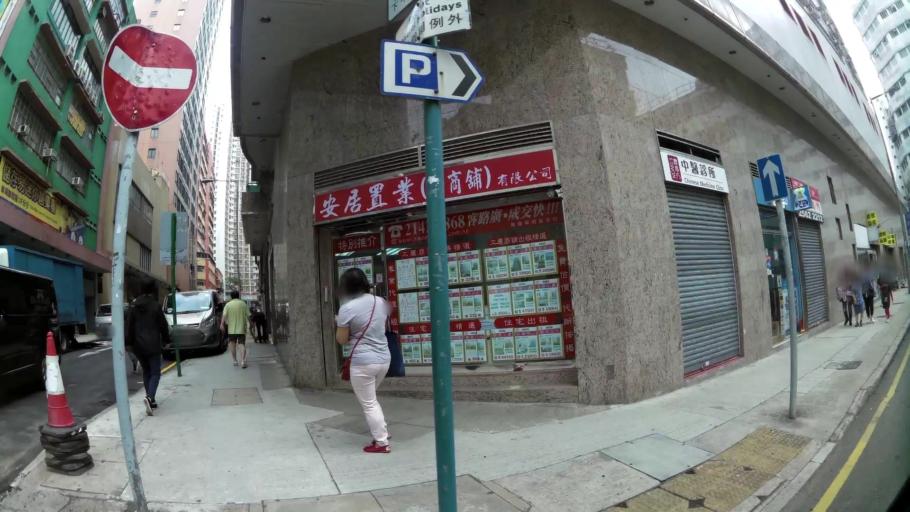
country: HK
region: Wanchai
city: Wan Chai
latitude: 22.2649
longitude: 114.2360
